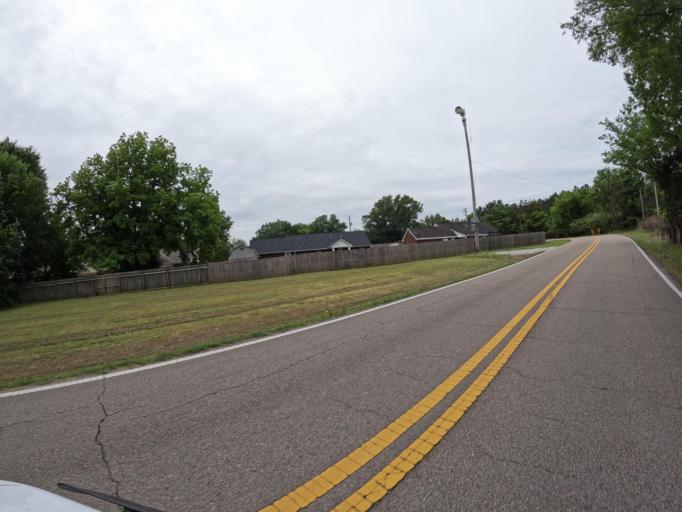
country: US
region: Mississippi
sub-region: Lee County
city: Tupelo
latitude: 34.2869
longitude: -88.7645
